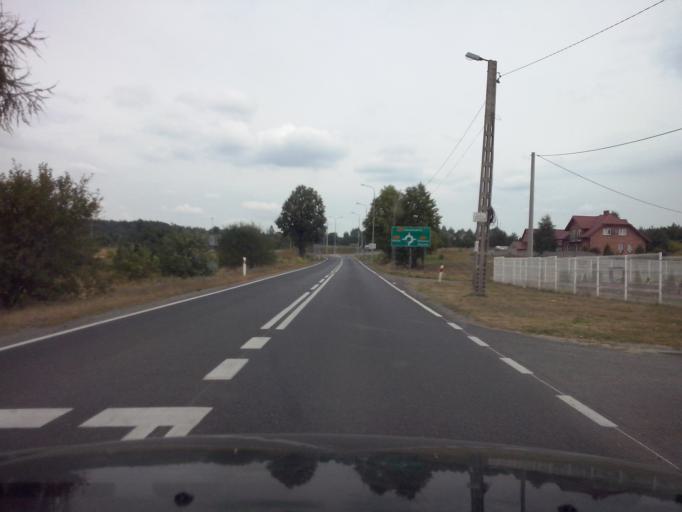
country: PL
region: Swietokrzyskie
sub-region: Powiat kielecki
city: Rakow
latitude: 50.6799
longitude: 21.0506
